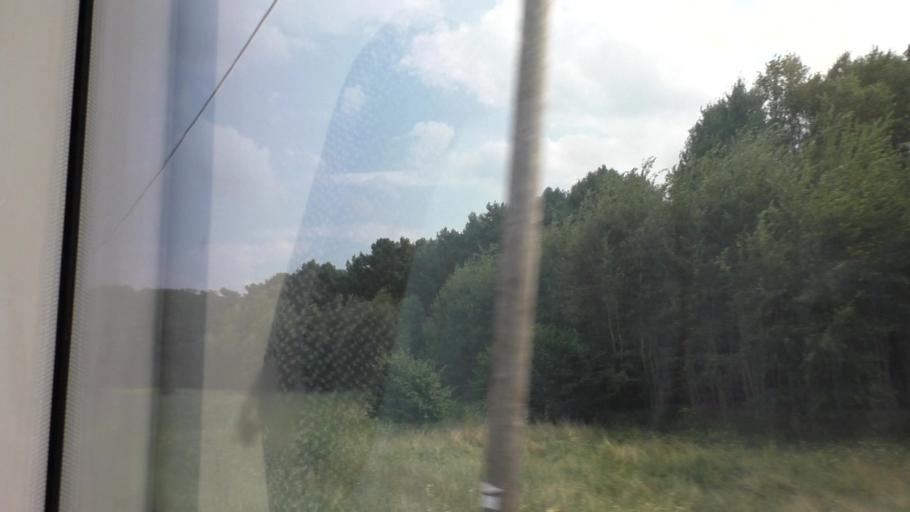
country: DE
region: Brandenburg
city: Spreenhagen
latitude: 52.2833
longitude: 13.8318
